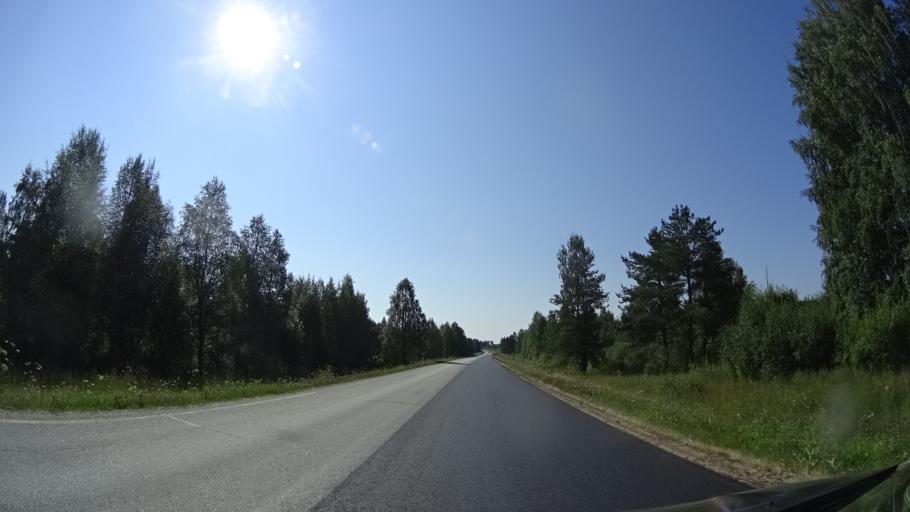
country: FI
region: North Karelia
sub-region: Joensuu
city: Juuka
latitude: 63.2376
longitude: 29.2824
